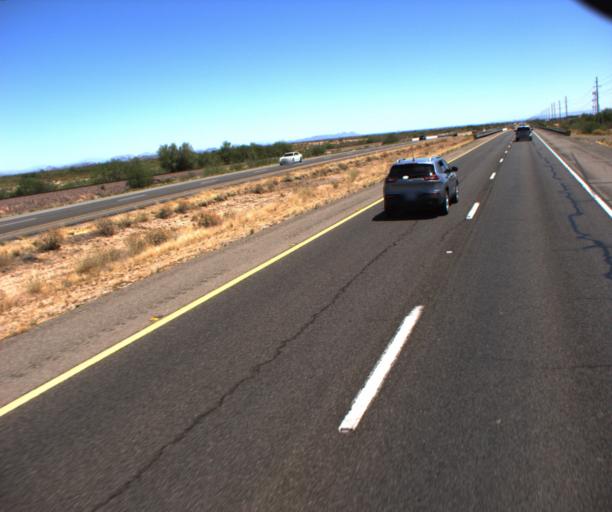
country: US
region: Arizona
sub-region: Maricopa County
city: Sun City West
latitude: 33.7491
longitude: -112.4920
